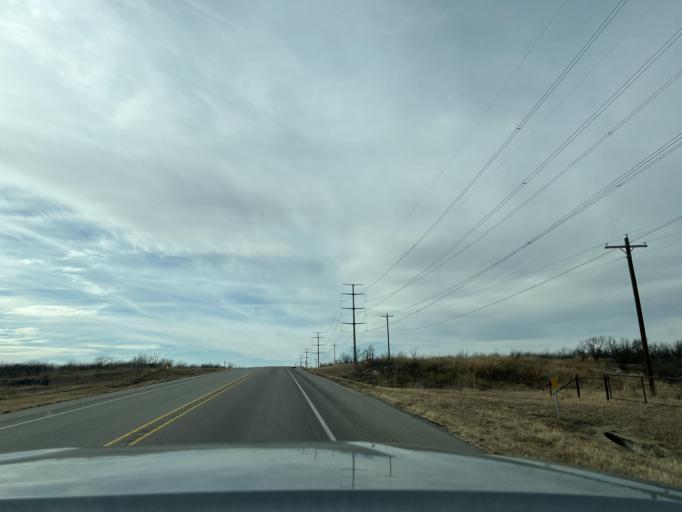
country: US
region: Texas
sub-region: Jones County
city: Stamford
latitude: 32.7503
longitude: -99.6398
